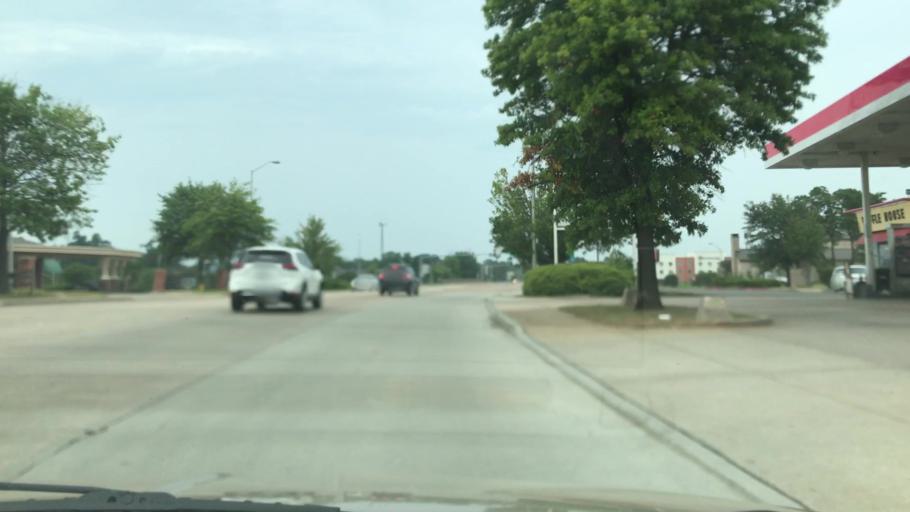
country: US
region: Louisiana
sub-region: Caddo Parish
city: Shreveport
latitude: 32.4594
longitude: -93.8274
